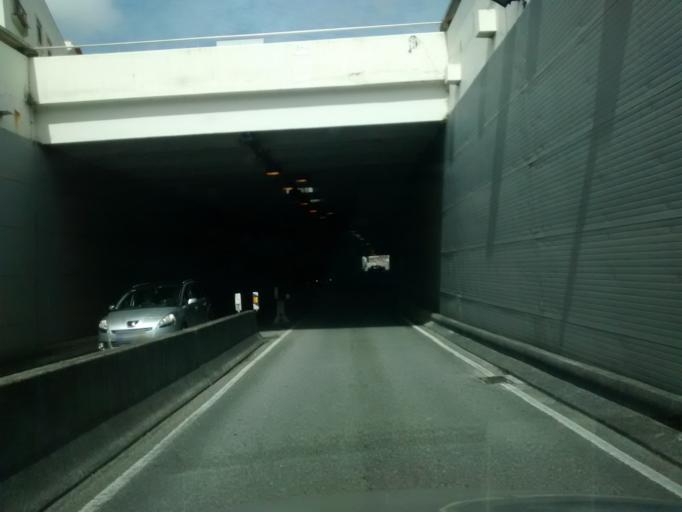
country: PT
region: Aveiro
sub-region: Aveiro
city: Aveiro
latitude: 40.6383
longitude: -8.6516
